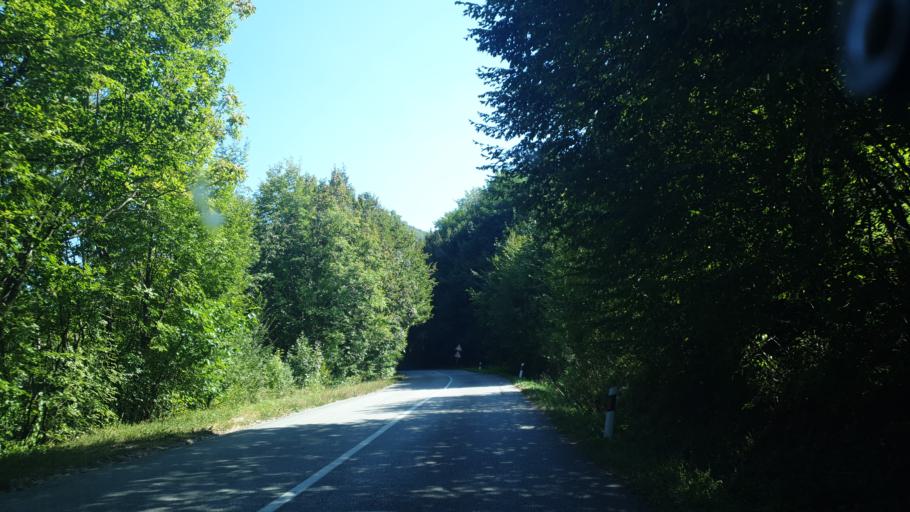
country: RS
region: Central Serbia
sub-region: Kolubarski Okrug
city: Mionica
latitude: 44.1558
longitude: 20.0066
